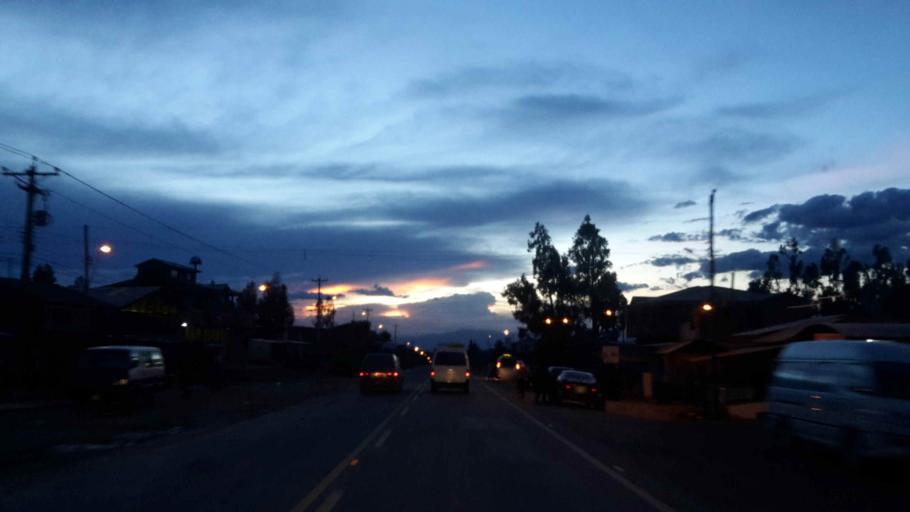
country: BO
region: Cochabamba
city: Colomi
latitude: -17.4200
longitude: -65.9441
